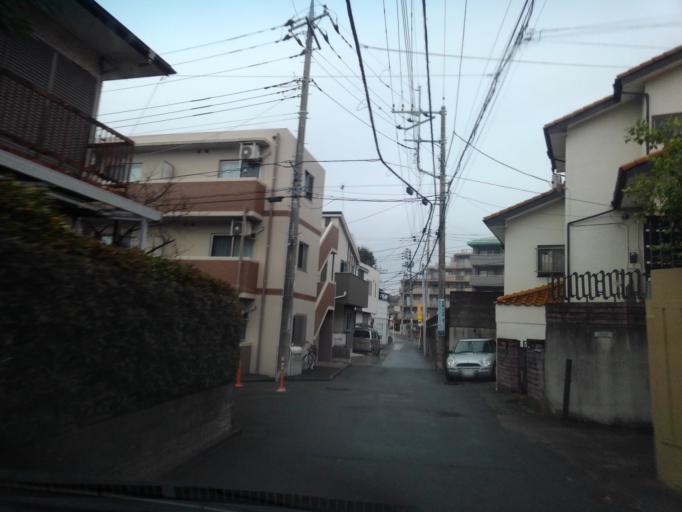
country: JP
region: Kanagawa
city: Minami-rinkan
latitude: 35.5104
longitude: 139.4424
